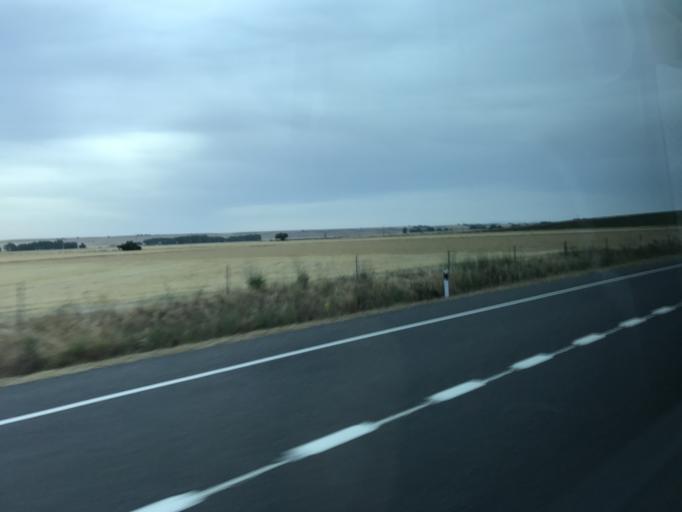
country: ES
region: Castille and Leon
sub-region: Provincia de Segovia
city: San Cristobal de la Vega
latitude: 41.1156
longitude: -4.6397
